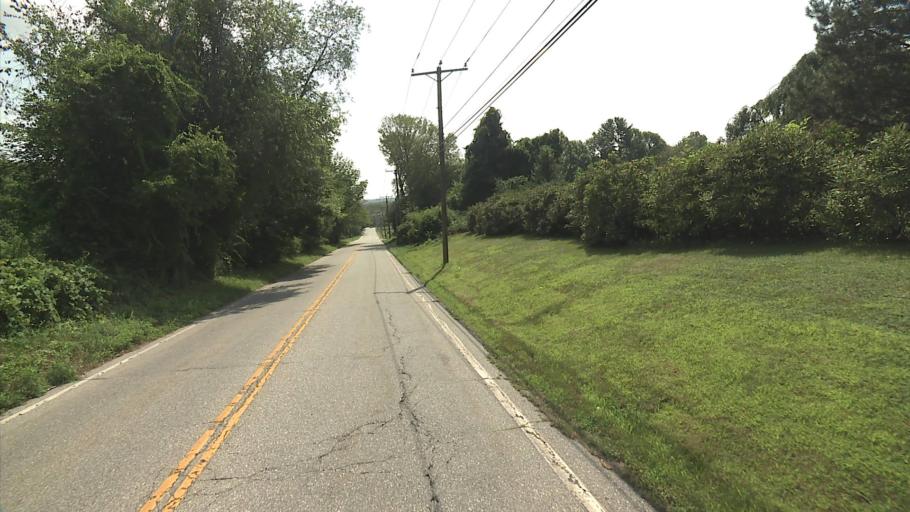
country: US
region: Connecticut
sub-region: New London County
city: Preston City
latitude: 41.5331
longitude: -72.0106
